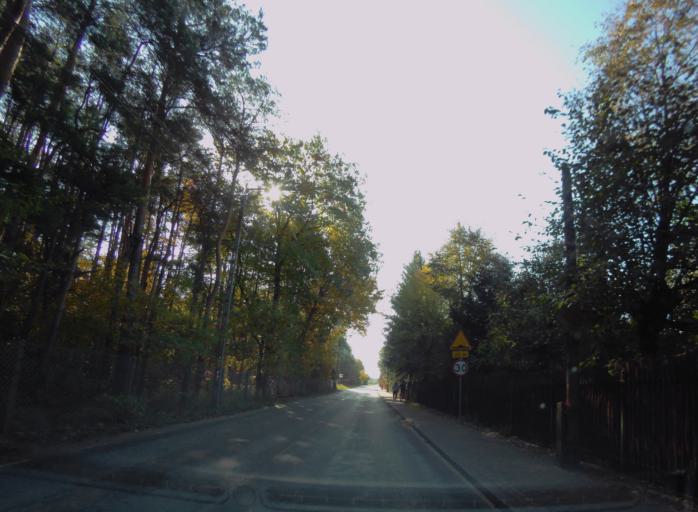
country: PL
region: Masovian Voivodeship
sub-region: Powiat otwocki
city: Jozefow
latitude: 52.1697
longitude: 21.3018
